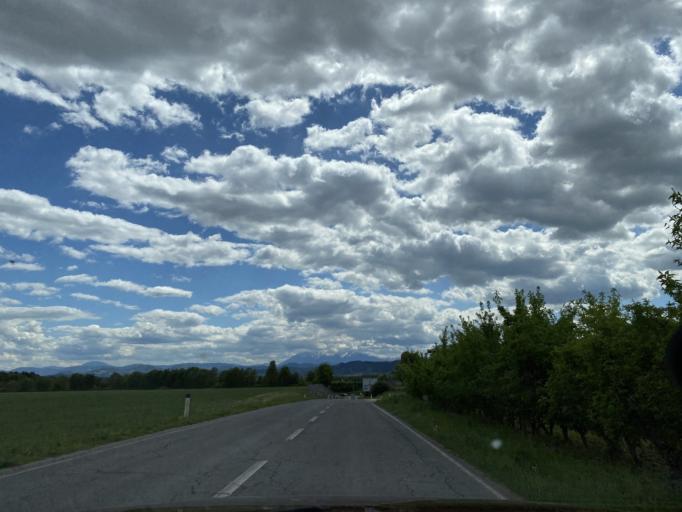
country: AT
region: Carinthia
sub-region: Politischer Bezirk Wolfsberg
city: Wolfsberg
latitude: 46.8259
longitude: 14.8270
